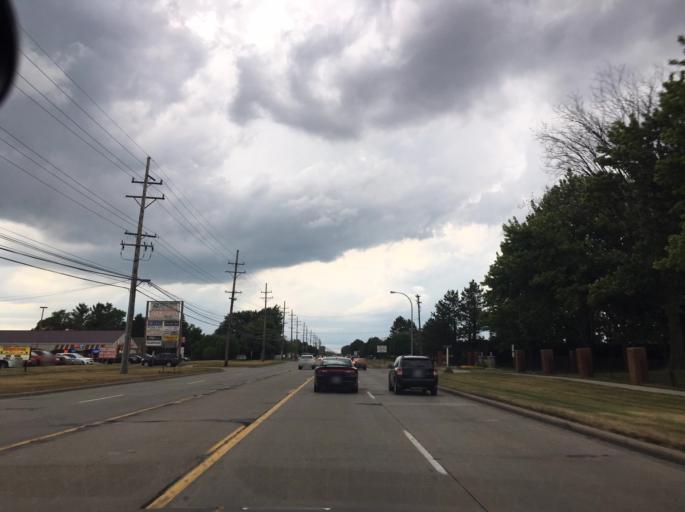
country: US
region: Michigan
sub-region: Macomb County
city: Clinton
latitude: 42.6073
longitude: -82.9527
